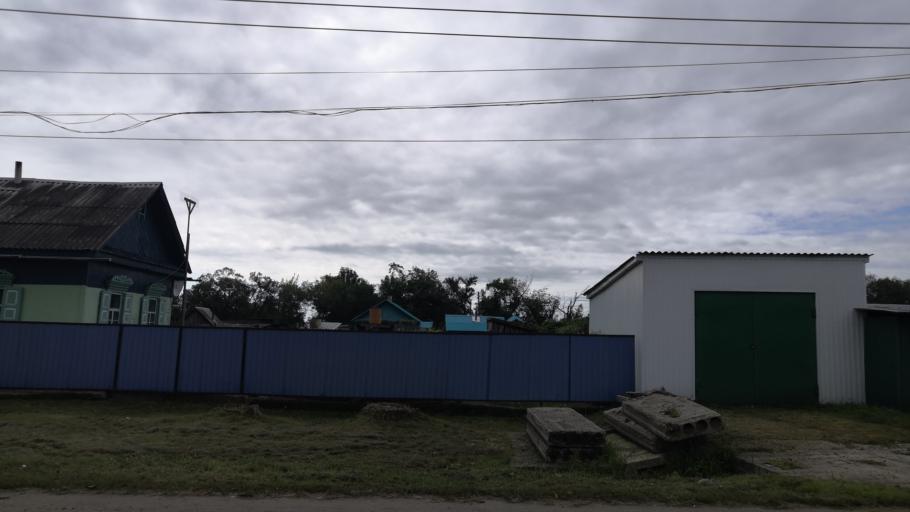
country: RU
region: Primorskiy
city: Dal'nerechensk
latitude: 45.9299
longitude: 133.7389
